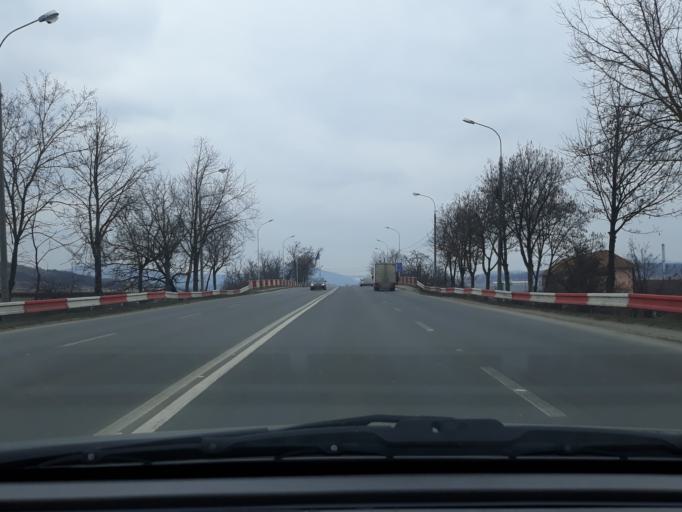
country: RO
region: Salaj
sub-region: Comuna Criseni
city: Criseni
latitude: 47.2189
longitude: 23.0410
